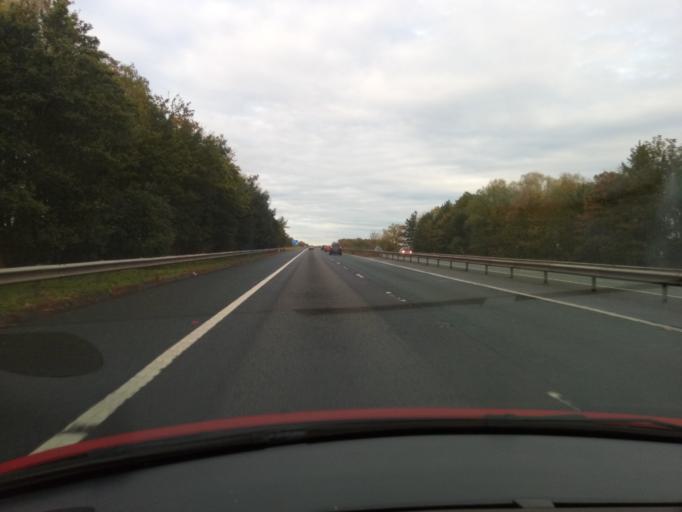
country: GB
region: England
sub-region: Darlington
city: High Coniscliffe
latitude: 54.5369
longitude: -1.6103
